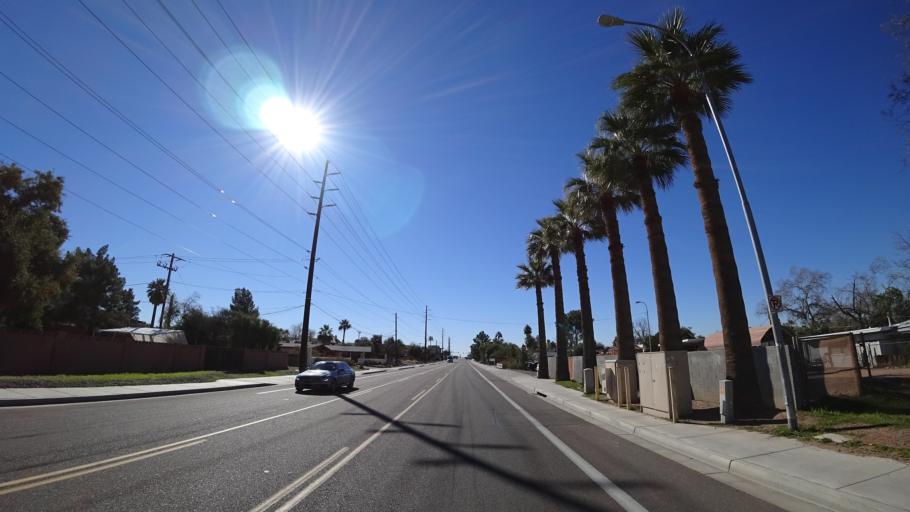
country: US
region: Arizona
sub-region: Maricopa County
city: Paradise Valley
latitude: 33.4764
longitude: -111.9697
